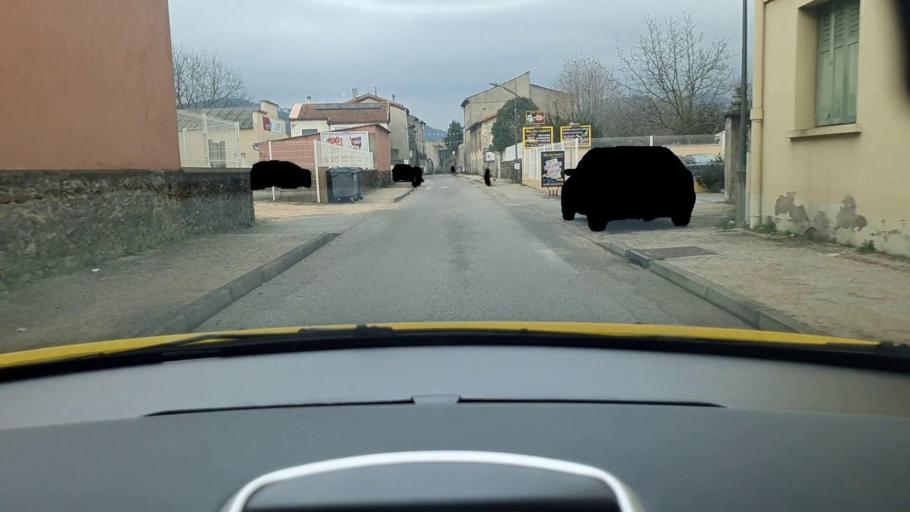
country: FR
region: Languedoc-Roussillon
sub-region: Departement du Gard
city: Besseges
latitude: 44.2874
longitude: 4.1086
